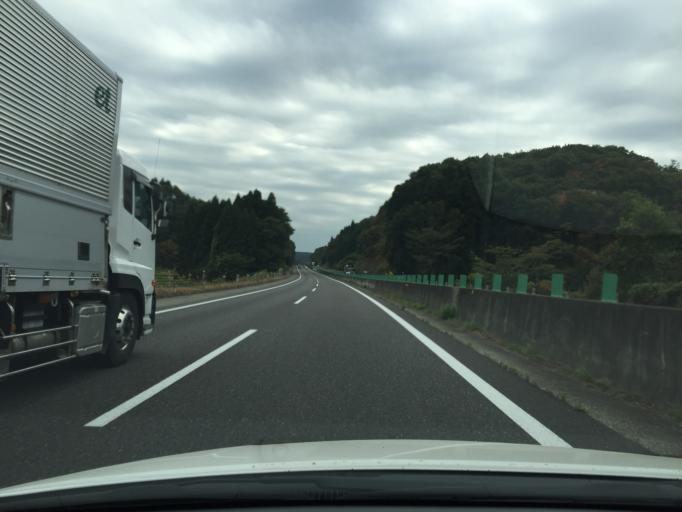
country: JP
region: Fukushima
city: Sukagawa
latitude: 37.1746
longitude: 140.2718
